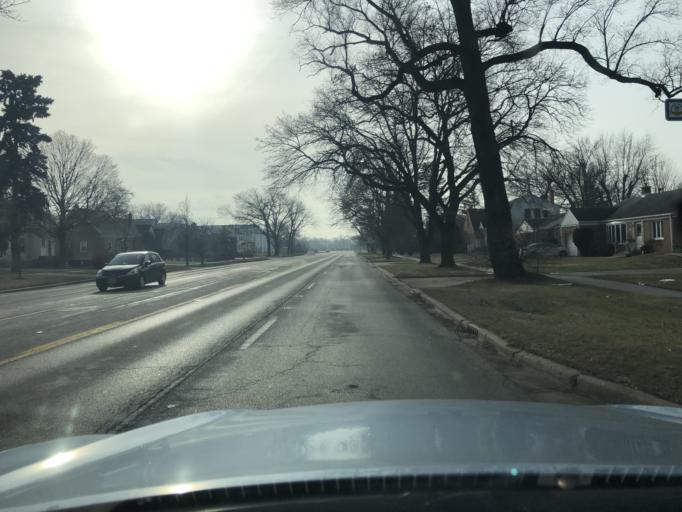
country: US
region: Illinois
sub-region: Cook County
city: Des Plaines
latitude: 42.0468
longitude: -87.9122
